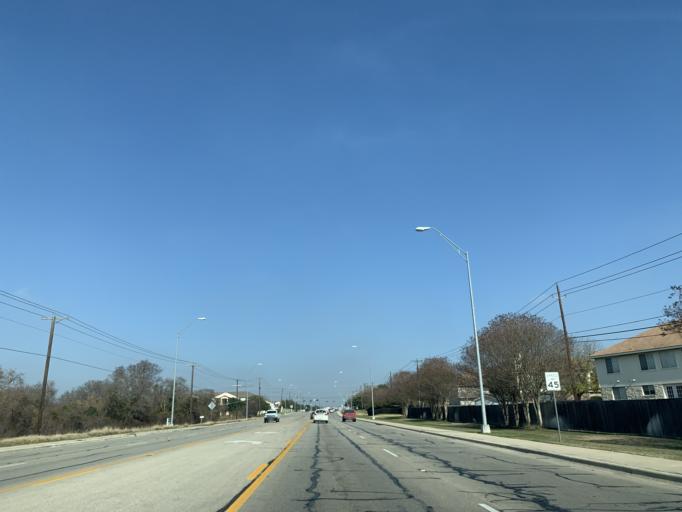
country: US
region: Texas
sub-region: Williamson County
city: Round Rock
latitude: 30.5365
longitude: -97.6517
